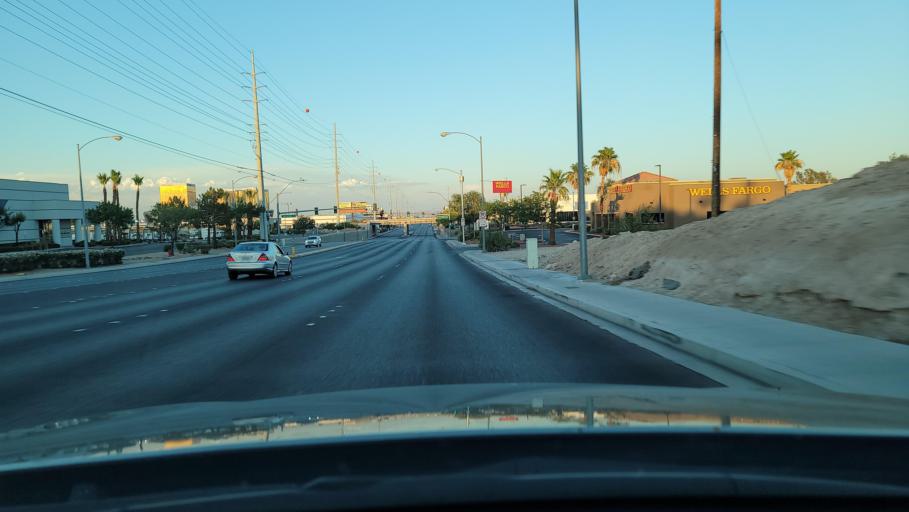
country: US
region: Nevada
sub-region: Clark County
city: Spring Valley
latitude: 36.0862
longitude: -115.2009
